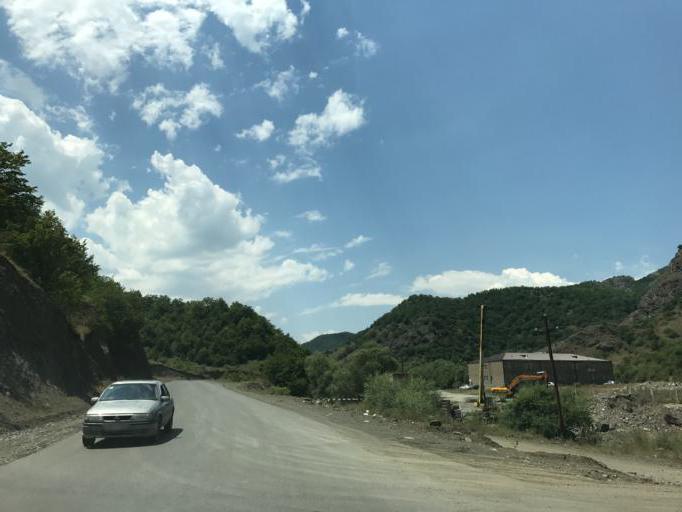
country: AZ
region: Kalbacar Rayonu
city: Kerbakhiar
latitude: 40.2294
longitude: 46.1598
